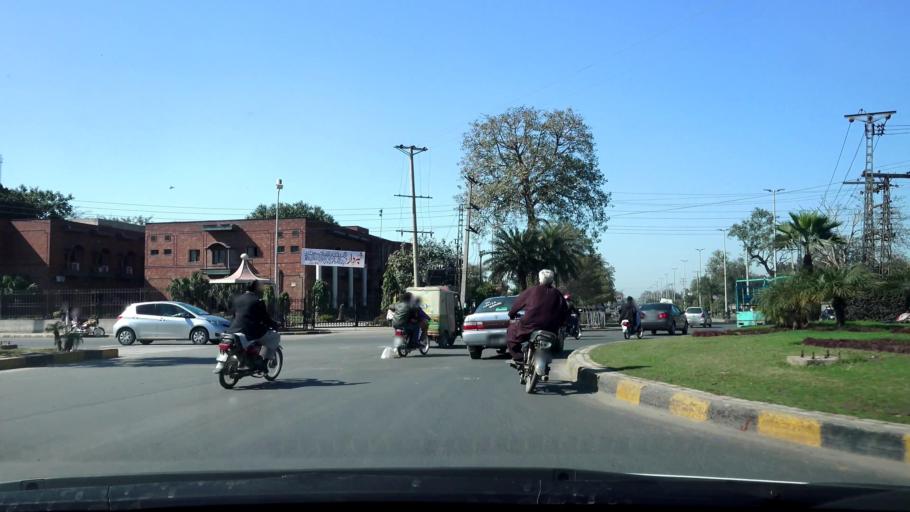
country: PK
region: Punjab
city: Faisalabad
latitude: 31.4194
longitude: 73.0875
